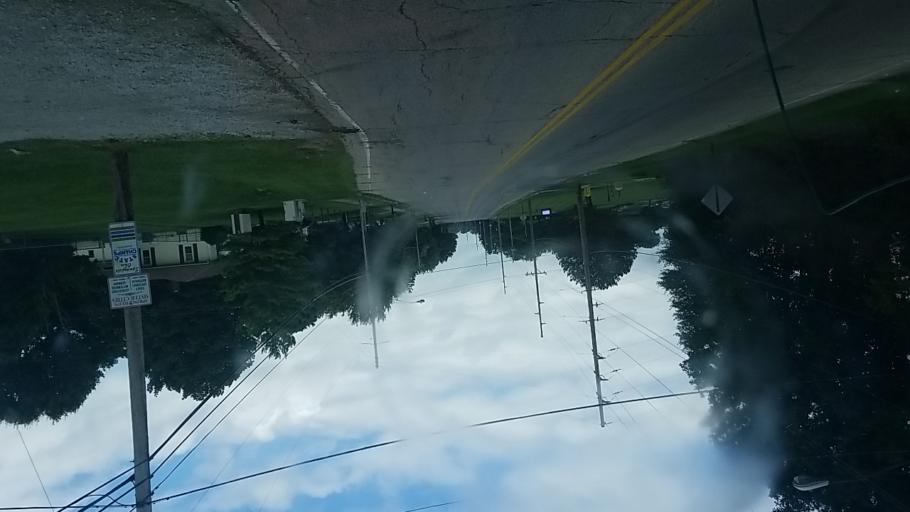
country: US
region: Ohio
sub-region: Clark County
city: Springfield
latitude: 39.8987
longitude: -83.7905
